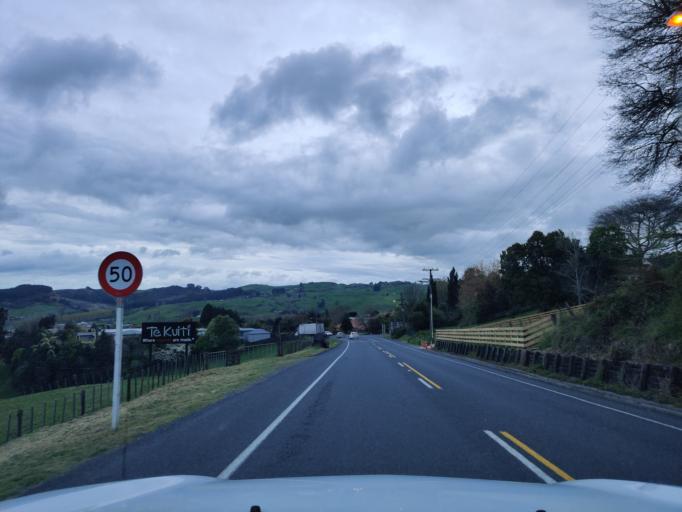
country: NZ
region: Waikato
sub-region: Otorohanga District
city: Otorohanga
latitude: -38.3485
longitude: 175.1660
